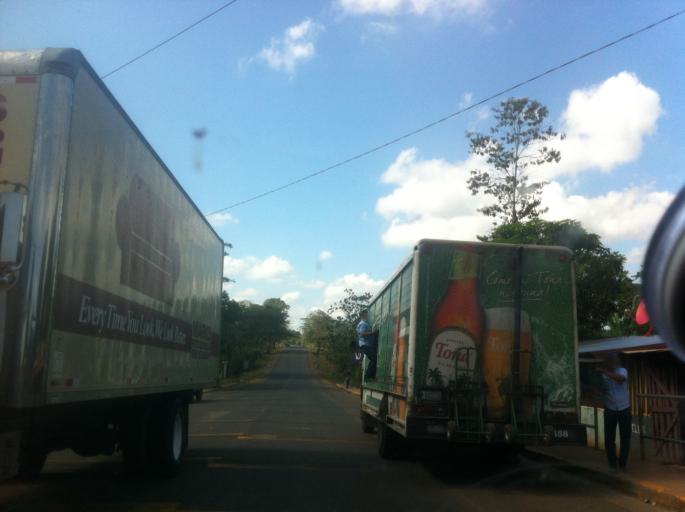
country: NI
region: Rio San Juan
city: San Carlos
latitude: 11.1934
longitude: -84.7425
